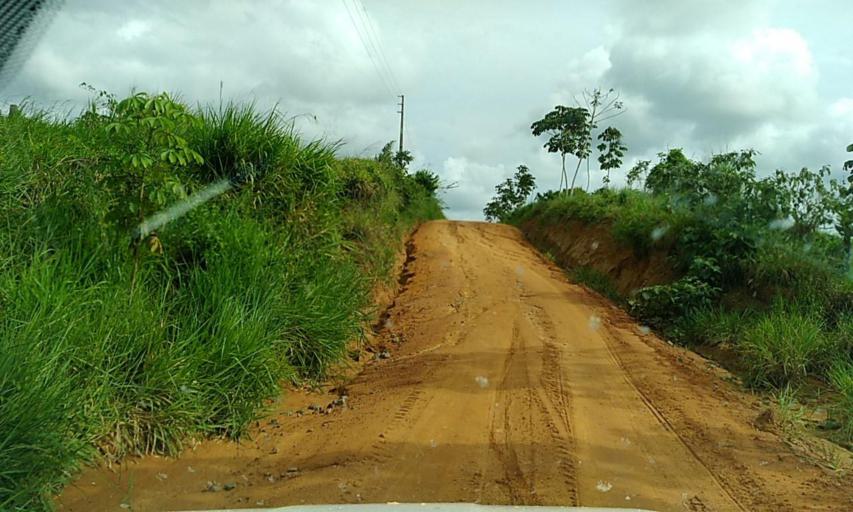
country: BR
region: Para
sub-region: Altamira
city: Altamira
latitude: -3.2607
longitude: -52.6940
